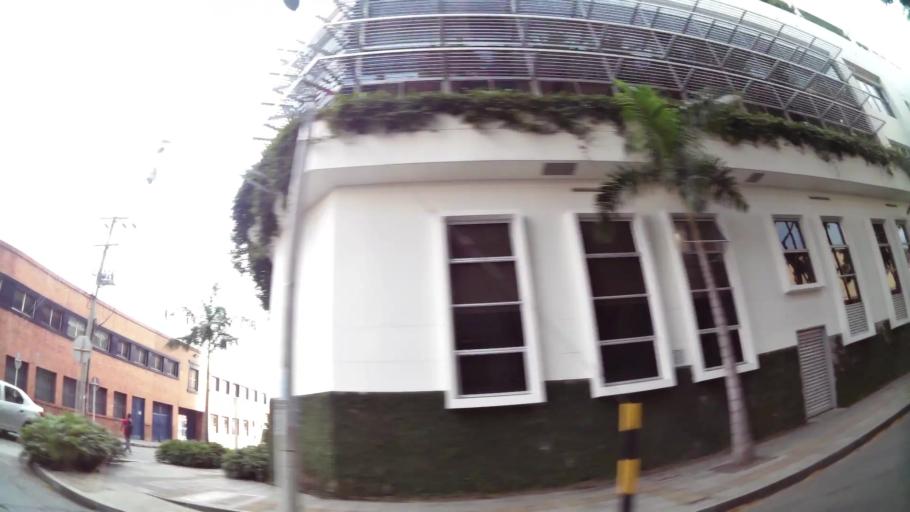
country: CO
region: Valle del Cauca
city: Cali
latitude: 3.4550
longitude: -76.5218
